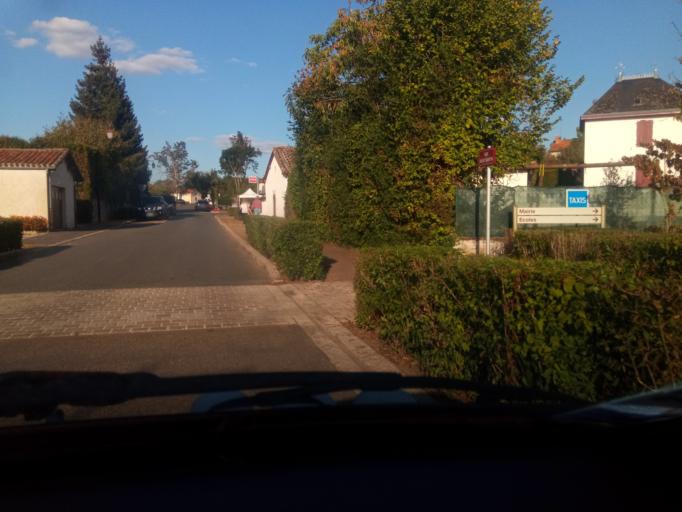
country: FR
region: Poitou-Charentes
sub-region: Departement de la Vienne
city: Availles-Limouzine
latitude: 46.1205
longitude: 0.7828
